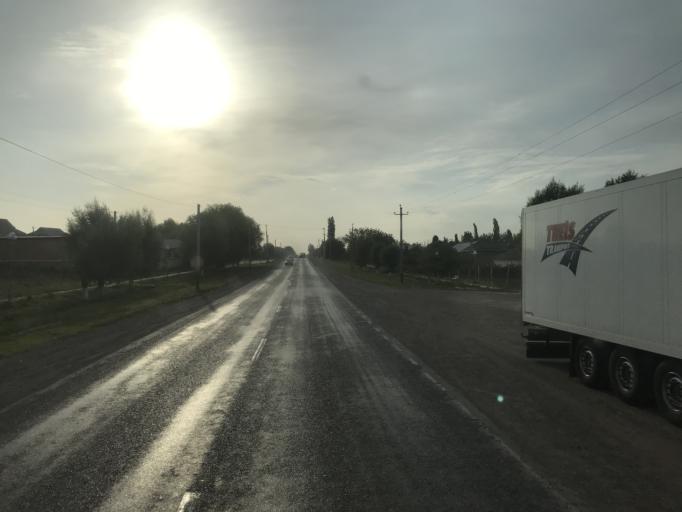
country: UZ
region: Toshkent
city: Salor
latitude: 41.4937
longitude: 69.3070
